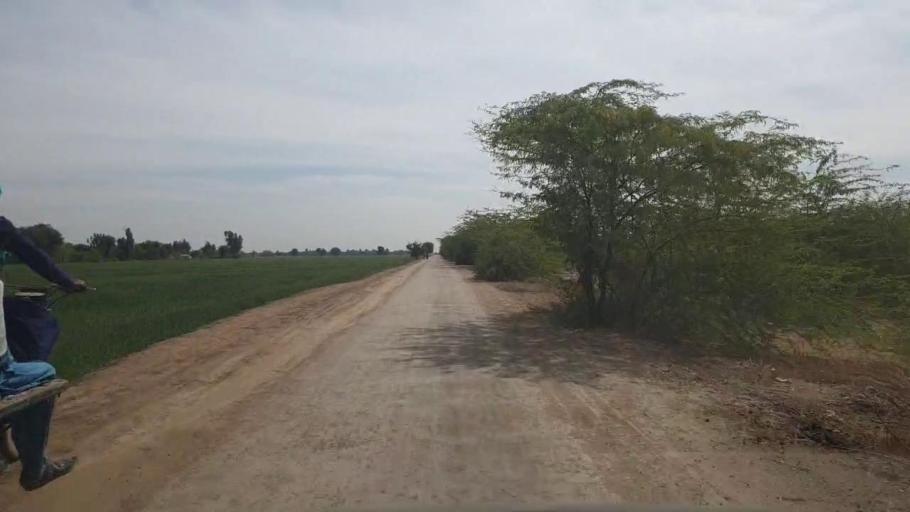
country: PK
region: Sindh
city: Kunri
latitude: 25.2846
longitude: 69.5946
